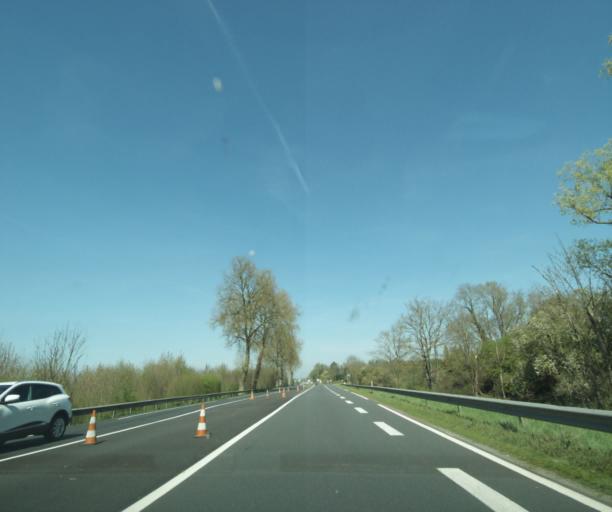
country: FR
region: Auvergne
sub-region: Departement de l'Allier
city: Trevol
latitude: 46.6278
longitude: 3.2845
